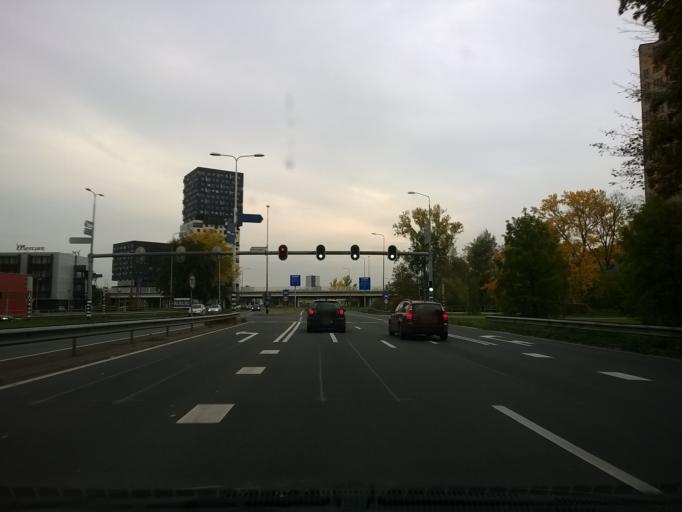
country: NL
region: Groningen
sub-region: Gemeente Groningen
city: Groningen
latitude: 53.2025
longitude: 6.5524
